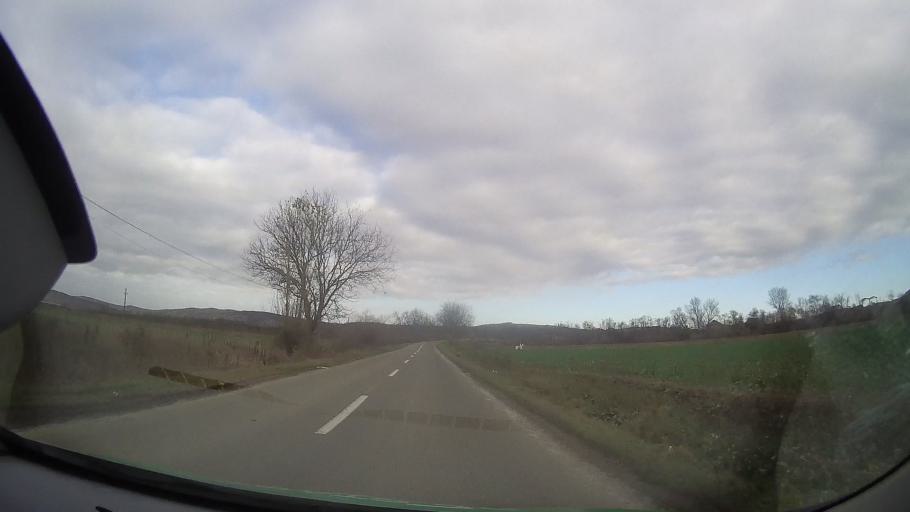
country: RO
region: Mures
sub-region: Comuna Iernut
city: Iernut
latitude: 46.4672
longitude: 24.2182
